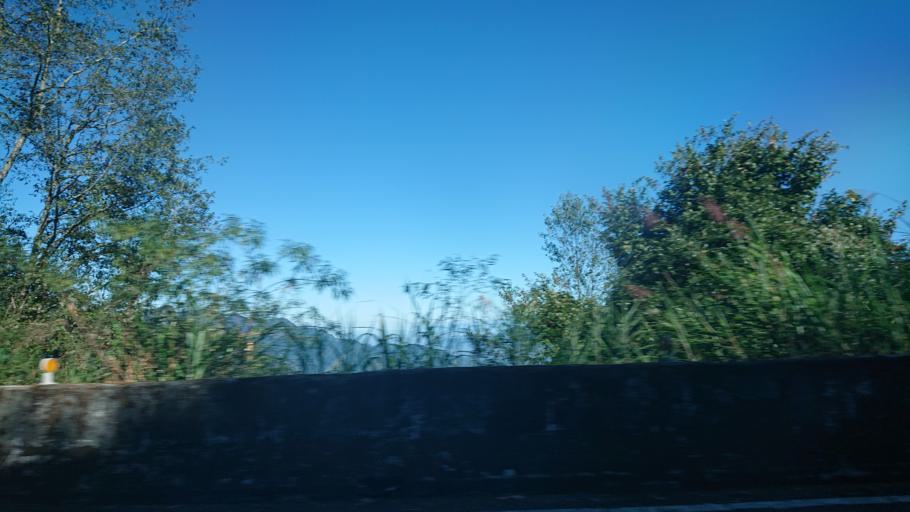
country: TW
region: Taiwan
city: Lugu
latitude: 23.4743
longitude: 120.8419
